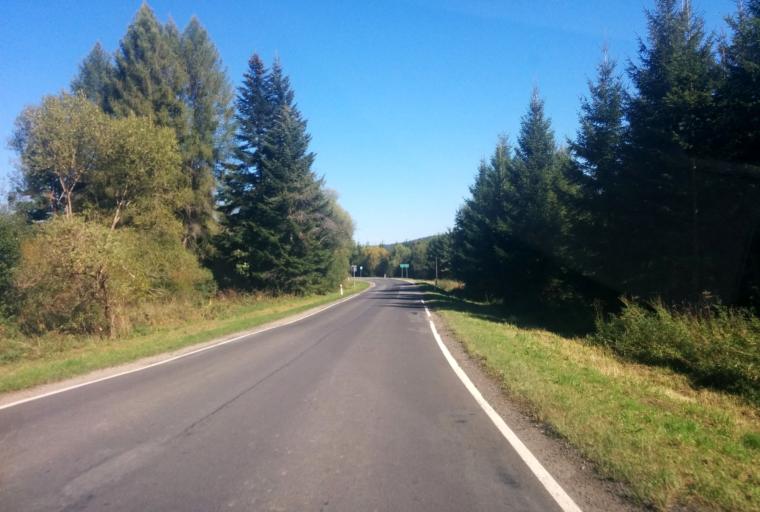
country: PL
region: Subcarpathian Voivodeship
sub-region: Powiat bieszczadzki
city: Czarna
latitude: 49.2976
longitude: 22.6690
